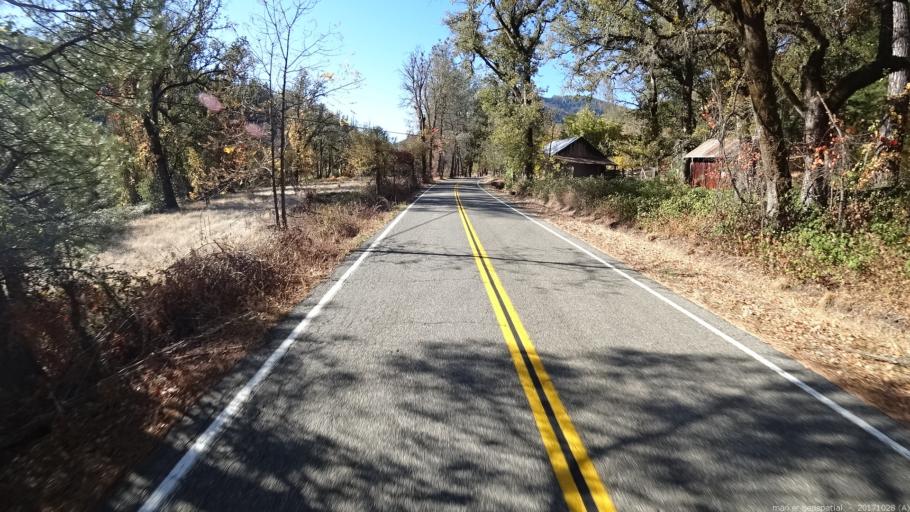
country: US
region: California
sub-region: Trinity County
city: Lewiston
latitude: 40.7516
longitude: -122.6173
